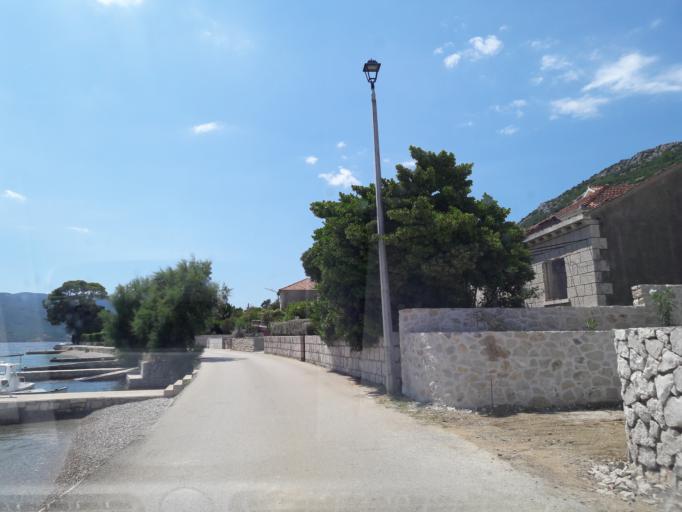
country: HR
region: Dubrovacko-Neretvanska
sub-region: Grad Korcula
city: Zrnovo
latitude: 42.9846
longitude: 17.0904
